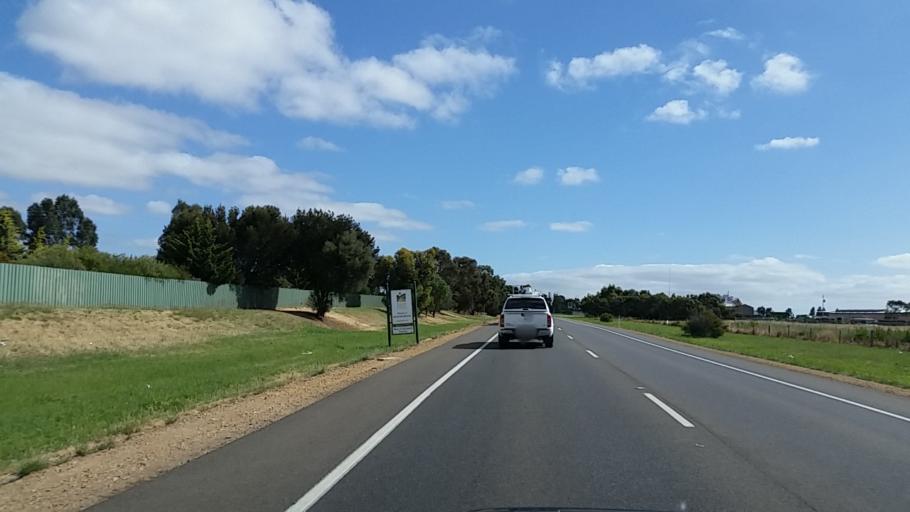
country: AU
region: South Australia
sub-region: Light
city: Roseworthy
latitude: -34.5392
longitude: 138.7499
